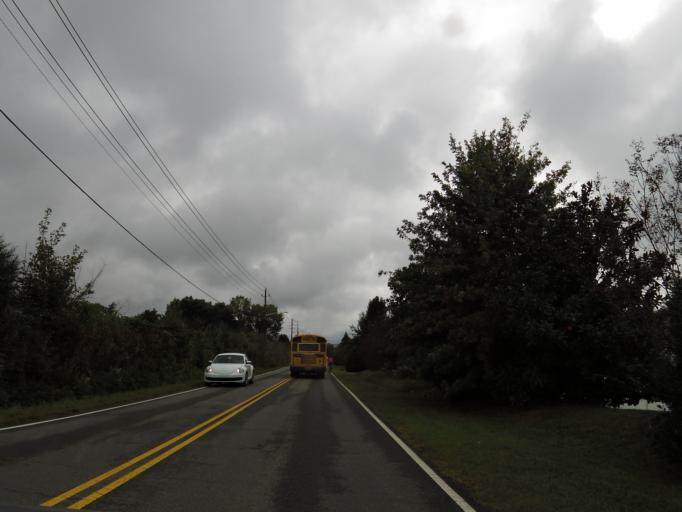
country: US
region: Tennessee
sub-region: Bradley County
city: Hopewell
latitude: 35.2029
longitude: -84.9055
